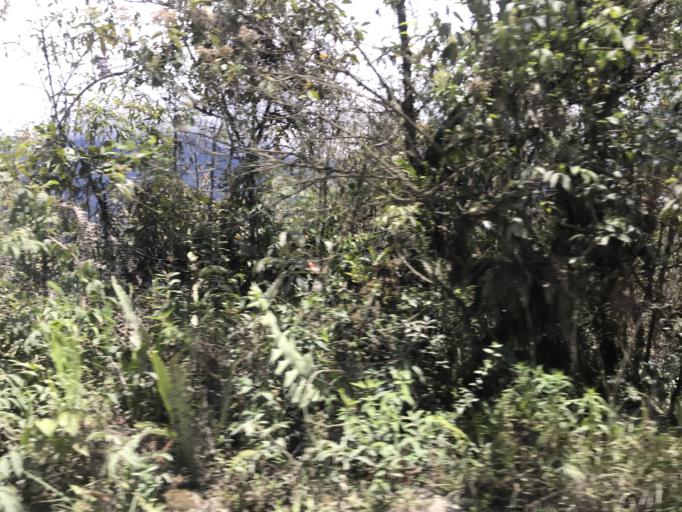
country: PE
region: Cusco
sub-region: Provincia de La Convencion
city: Santa Teresa
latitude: -13.1664
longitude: -72.5409
